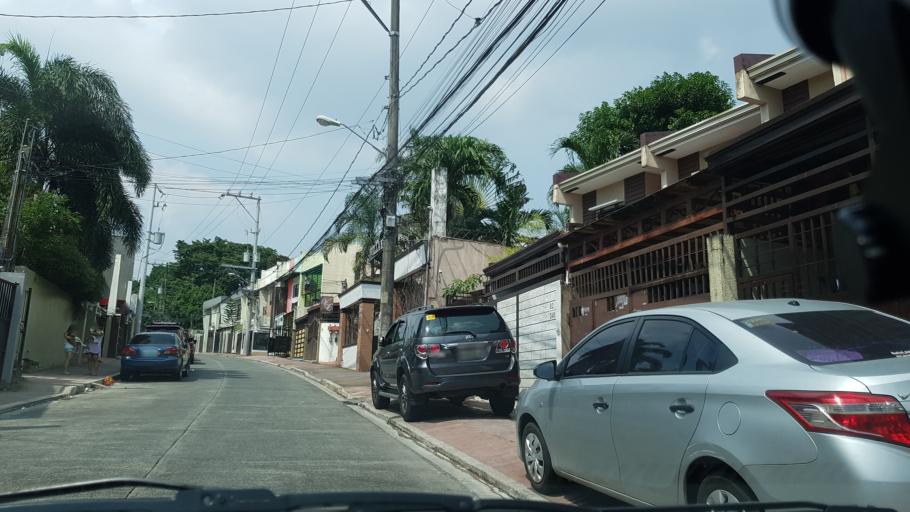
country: PH
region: Calabarzon
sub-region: Province of Rizal
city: Antipolo
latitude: 14.6519
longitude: 121.1202
